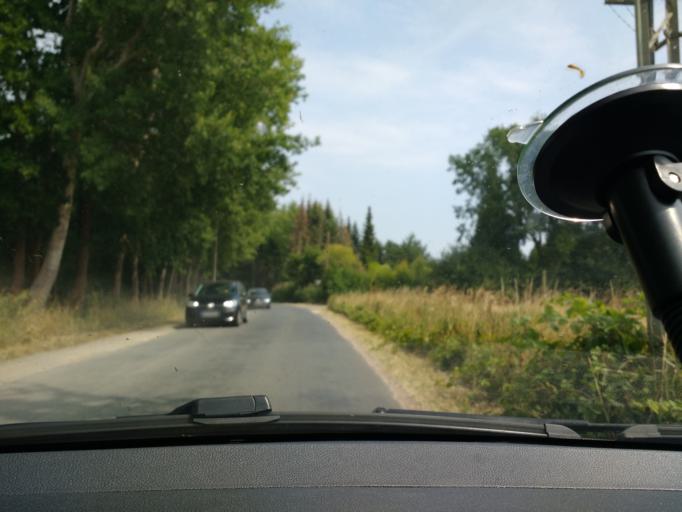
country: DE
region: Lower Saxony
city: Wagenhoff
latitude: 52.5169
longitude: 10.5510
